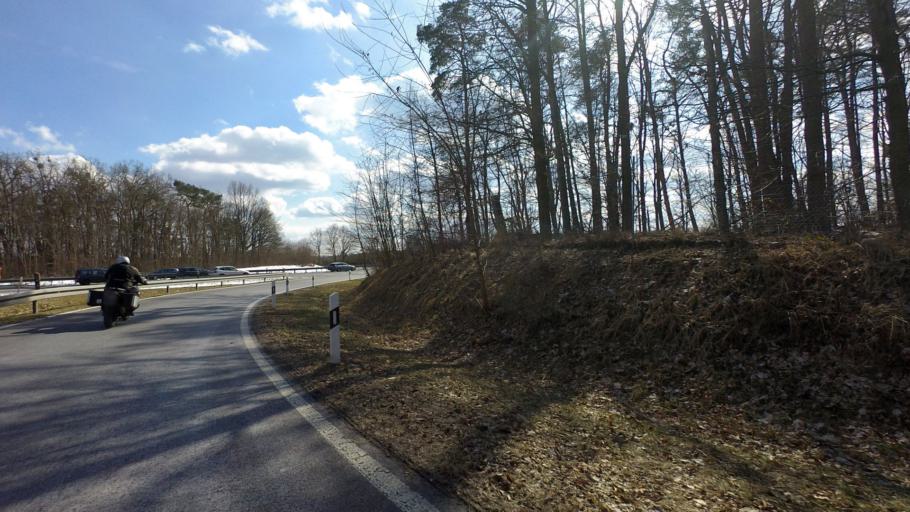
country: DE
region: Brandenburg
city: Joachimsthal
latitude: 52.8919
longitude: 13.7168
